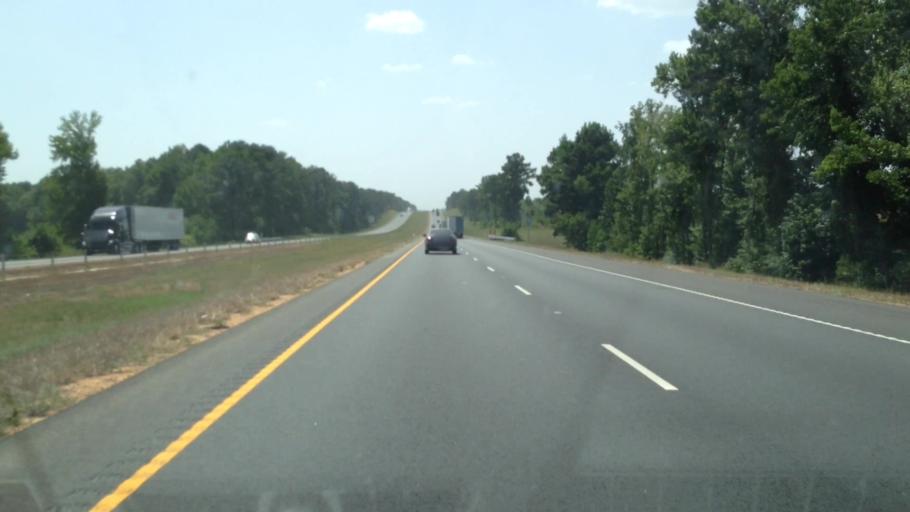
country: US
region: Louisiana
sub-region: Webster Parish
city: Minden
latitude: 32.5819
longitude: -93.2543
